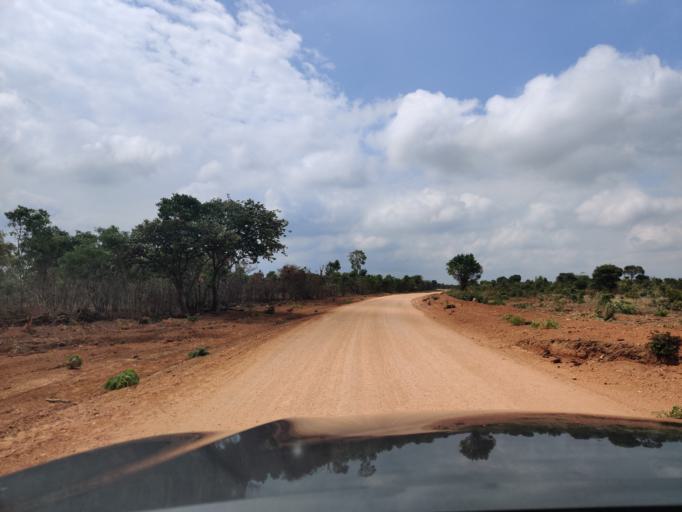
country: ZM
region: Central
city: Mkushi
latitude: -13.6606
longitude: 29.7520
